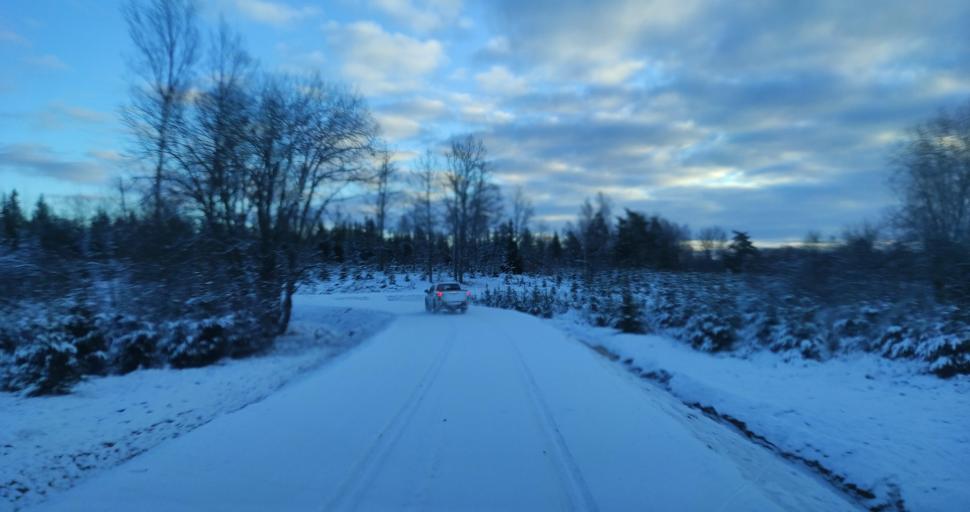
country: LV
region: Skrunda
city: Skrunda
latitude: 56.5851
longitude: 21.9508
